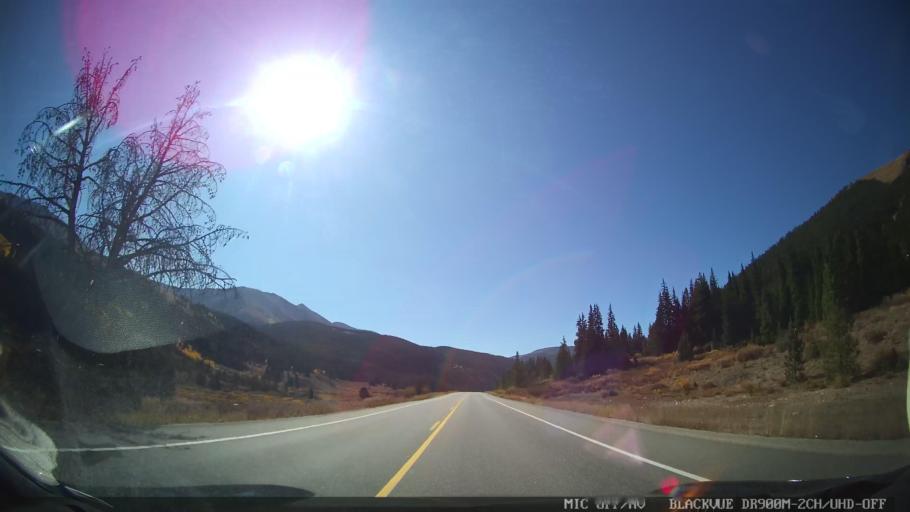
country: US
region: Colorado
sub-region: Lake County
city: Leadville
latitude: 39.3398
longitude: -106.2212
